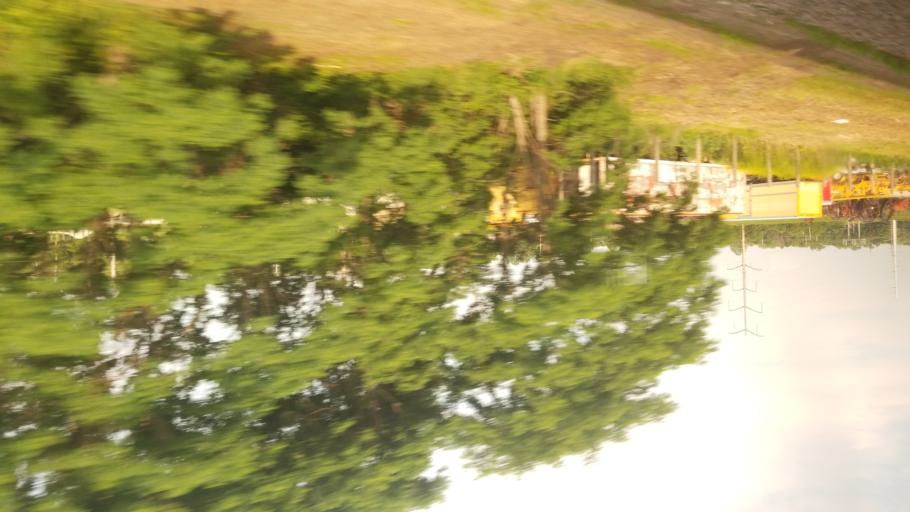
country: US
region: Illinois
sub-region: Kendall County
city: Oswego
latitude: 41.7062
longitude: -88.3641
